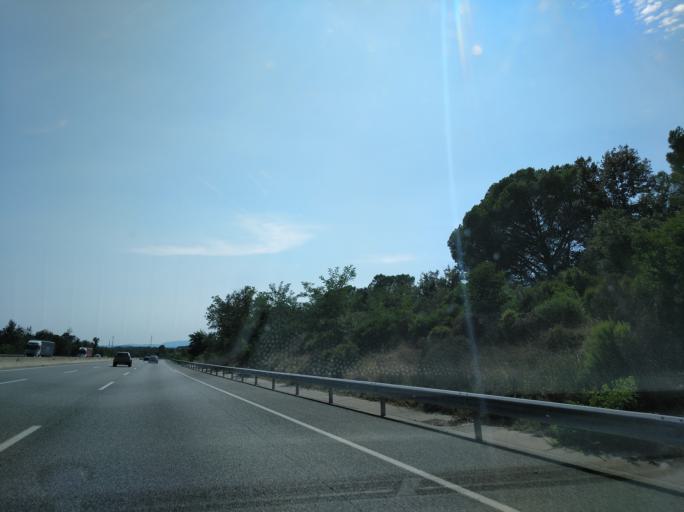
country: ES
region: Catalonia
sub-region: Provincia de Girona
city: Vilobi d'Onyar
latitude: 41.8563
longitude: 2.7524
